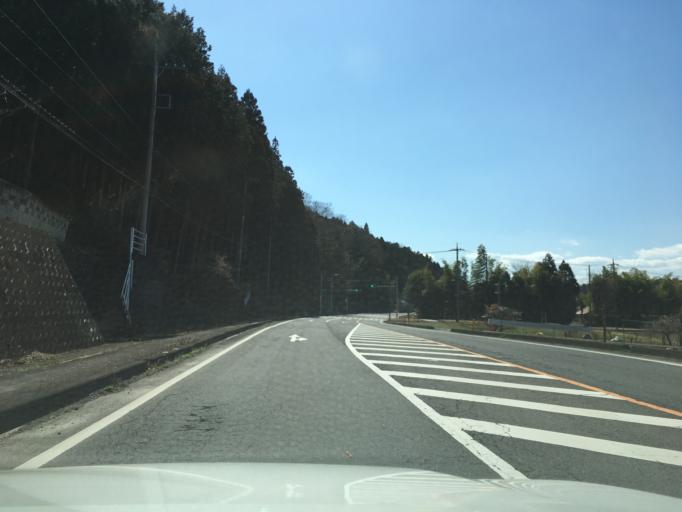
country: JP
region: Tochigi
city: Kuroiso
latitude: 36.9453
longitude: 140.1451
